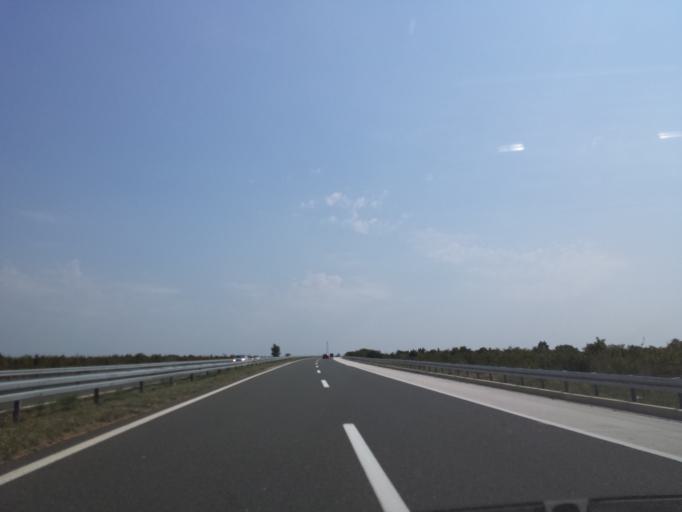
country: HR
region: Sibensko-Kniniska
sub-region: Grad Sibenik
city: Pirovac
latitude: 43.9207
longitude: 15.7374
